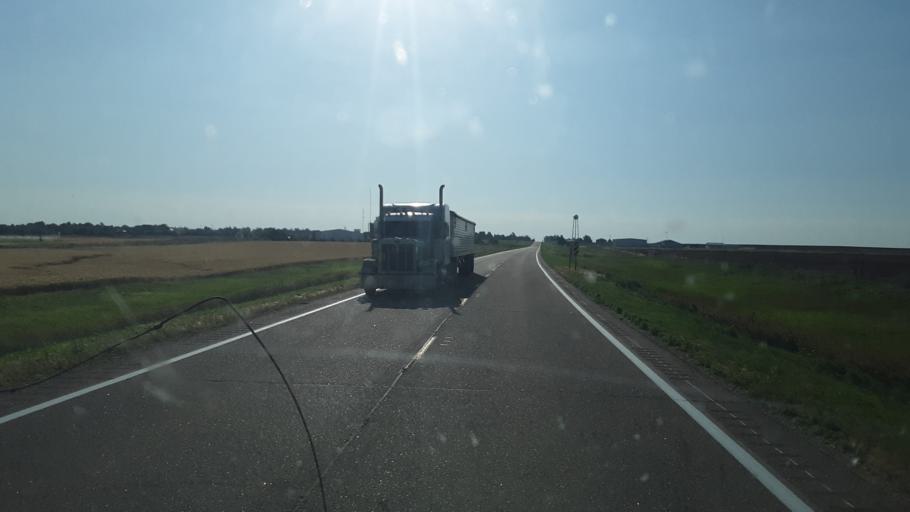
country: US
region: Kansas
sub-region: Edwards County
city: Kinsley
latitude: 38.1896
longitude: -99.5418
